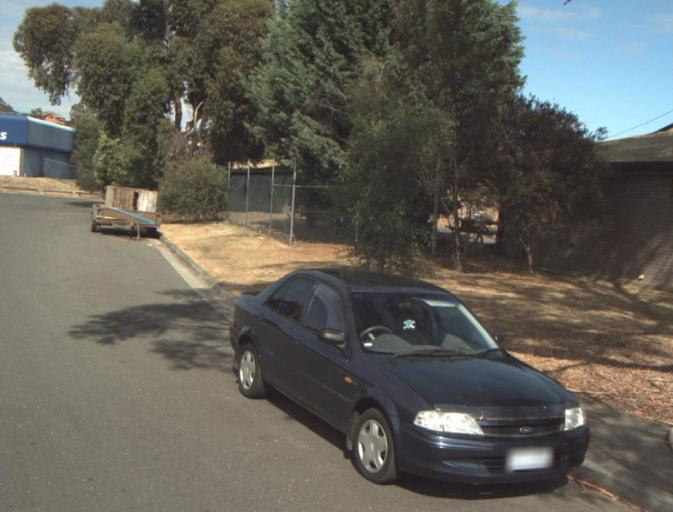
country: AU
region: Tasmania
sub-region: Launceston
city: Summerhill
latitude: -41.4712
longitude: 147.1366
